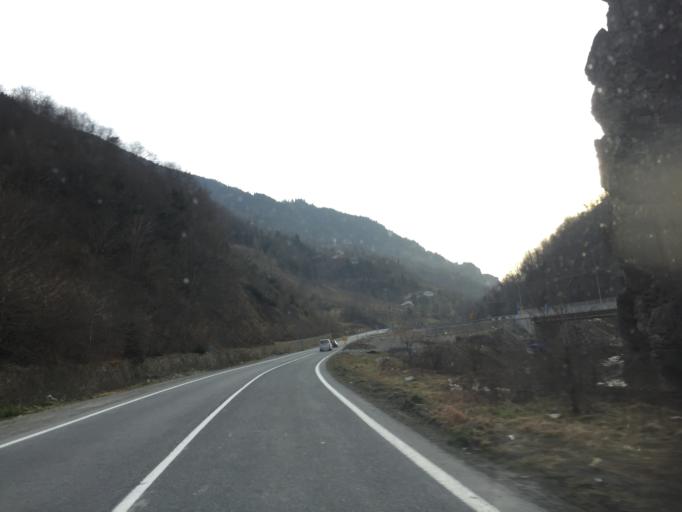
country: TR
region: Trabzon
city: Macka
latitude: 40.7482
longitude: 39.5622
